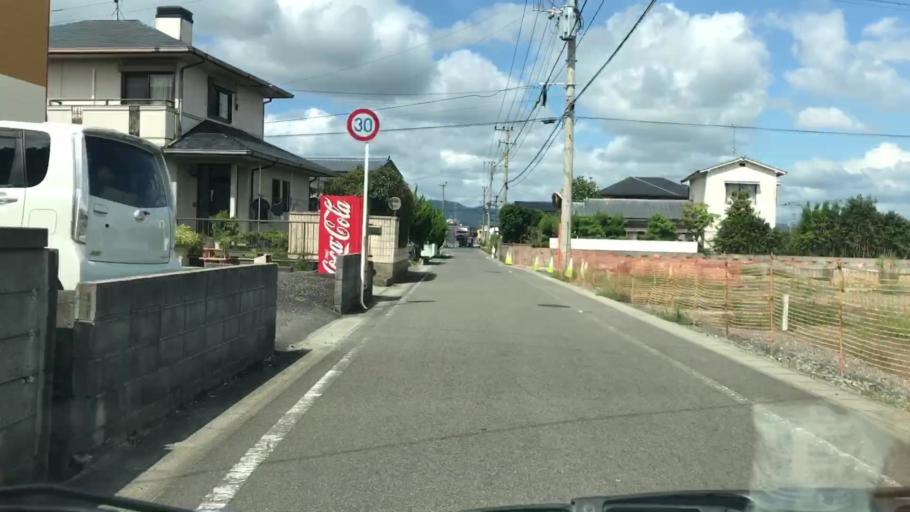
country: JP
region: Saga Prefecture
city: Saga-shi
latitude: 33.2421
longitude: 130.2017
